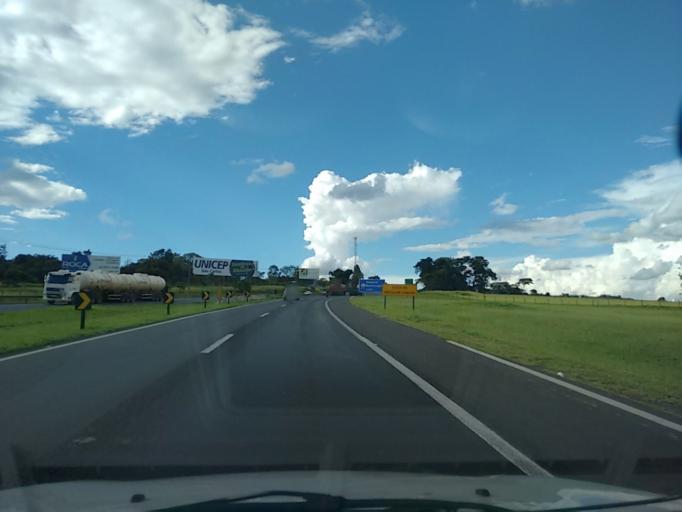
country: BR
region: Sao Paulo
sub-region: Sao Carlos
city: Sao Carlos
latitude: -22.0436
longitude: -47.8619
